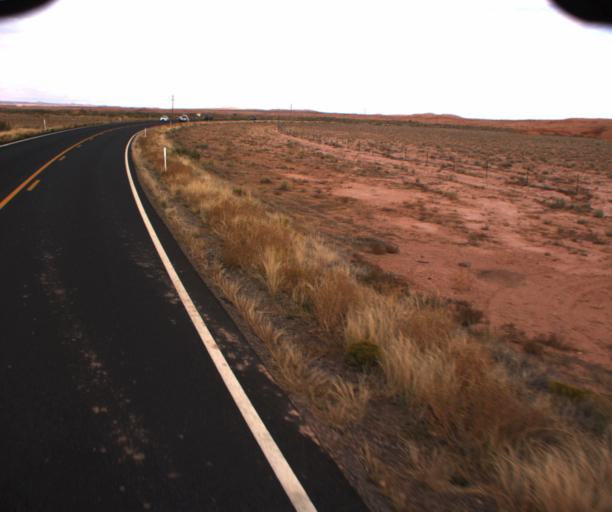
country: US
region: Arizona
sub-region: Apache County
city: Many Farms
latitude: 36.7708
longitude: -109.6602
